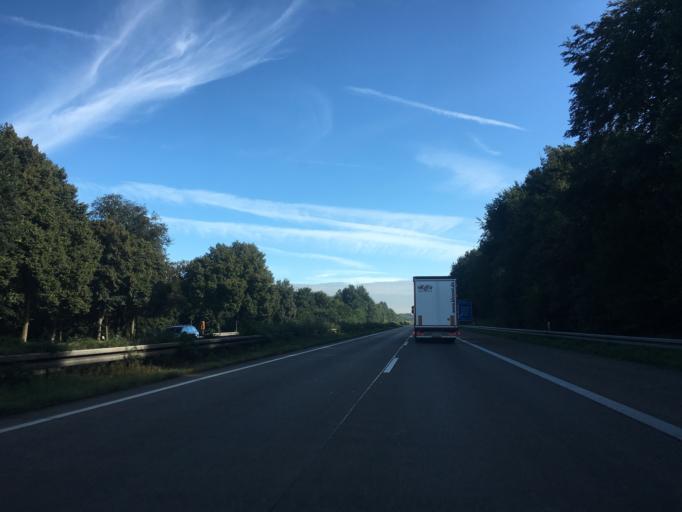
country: DE
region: North Rhine-Westphalia
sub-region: Regierungsbezirk Munster
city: Ladbergen
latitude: 52.1368
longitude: 7.7244
